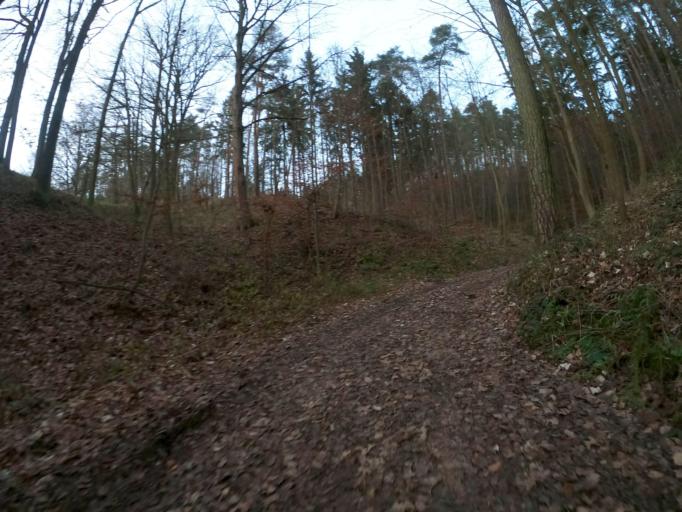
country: DE
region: Thuringia
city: Laasdorf
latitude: 50.8819
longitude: 11.6663
